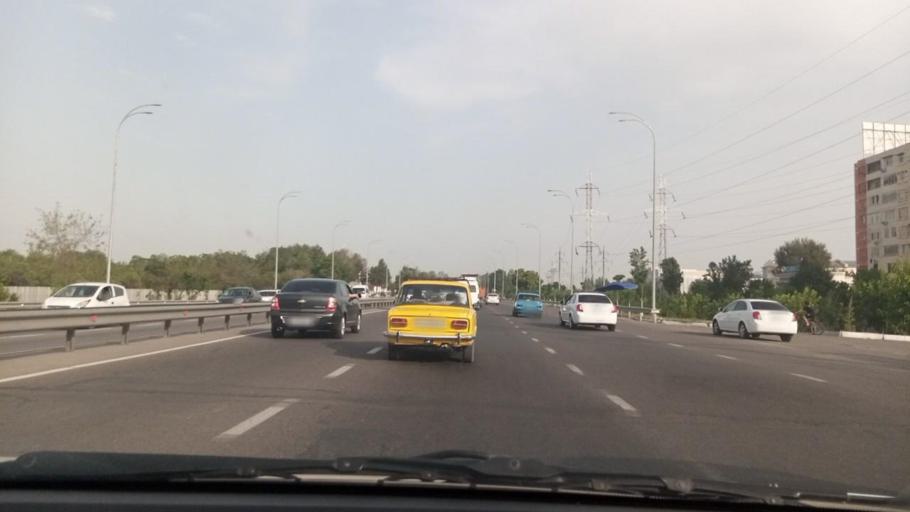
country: UZ
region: Toshkent Shahri
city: Bektemir
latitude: 41.2571
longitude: 69.3802
